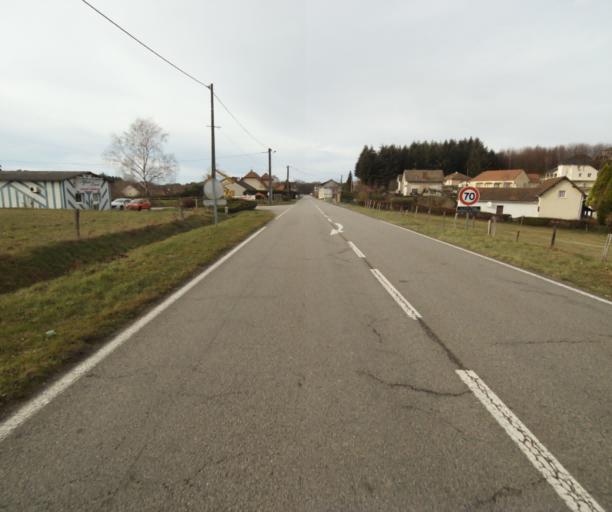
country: FR
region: Limousin
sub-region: Departement de la Correze
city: Saint-Mexant
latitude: 45.2718
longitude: 1.6846
